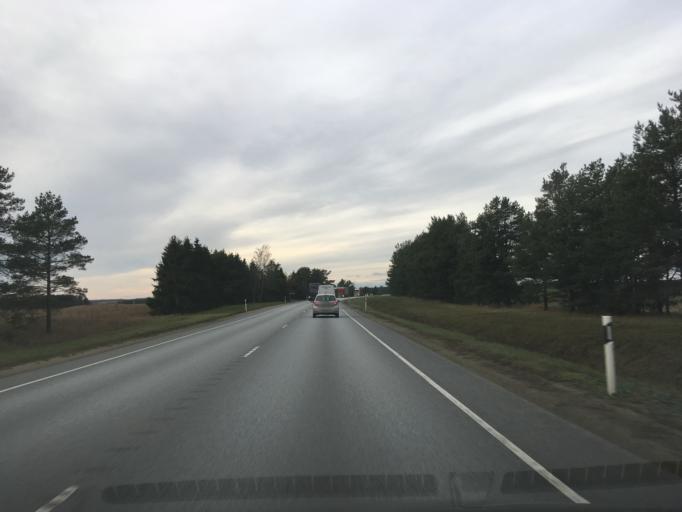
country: EE
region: Ida-Virumaa
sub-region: Puessi linn
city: Pussi
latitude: 59.4060
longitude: 27.0610
